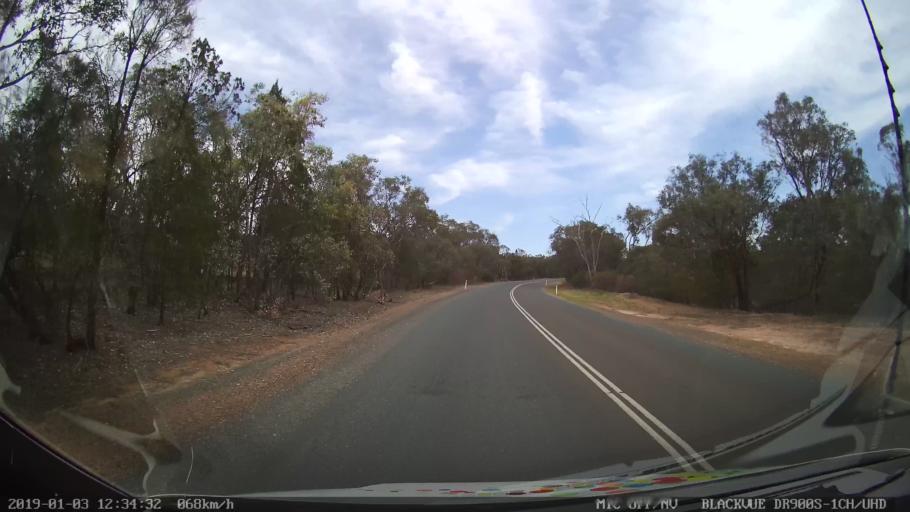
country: AU
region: New South Wales
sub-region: Weddin
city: Grenfell
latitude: -33.8755
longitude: 148.1663
